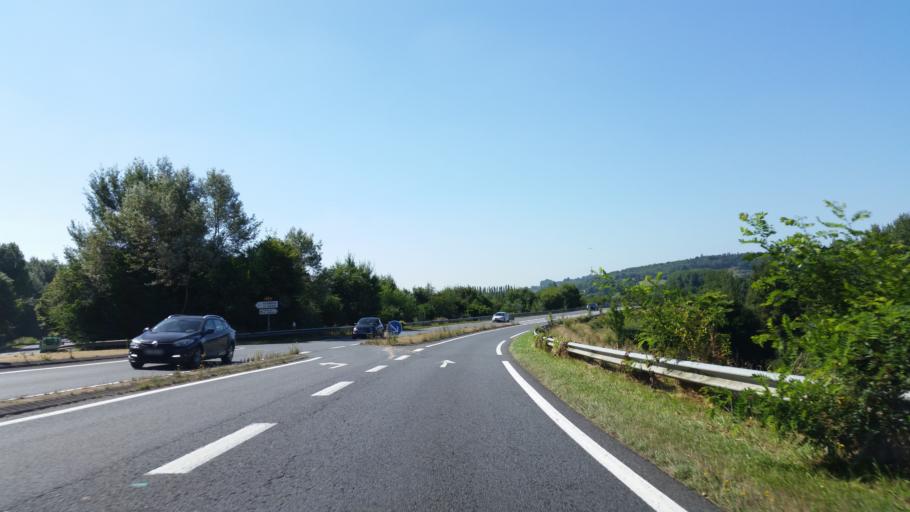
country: FR
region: Lower Normandy
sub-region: Departement du Calvados
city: Lisieux
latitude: 49.2379
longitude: 0.2223
